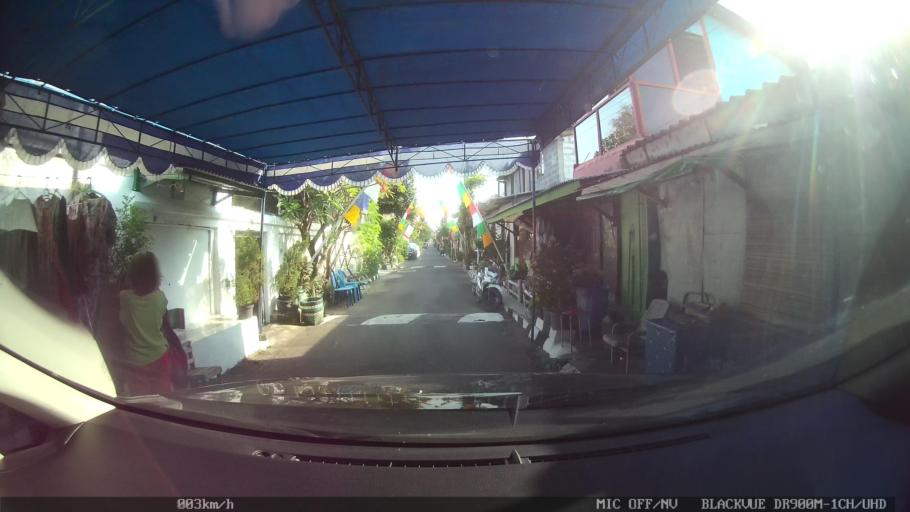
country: ID
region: Daerah Istimewa Yogyakarta
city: Yogyakarta
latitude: -7.8138
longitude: 110.3683
